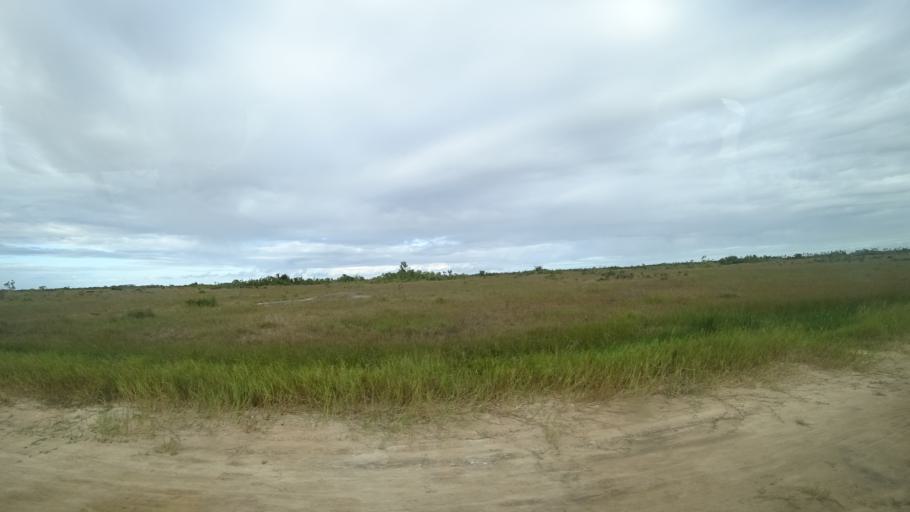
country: MZ
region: Sofala
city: Beira
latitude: -19.6995
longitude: 35.0283
